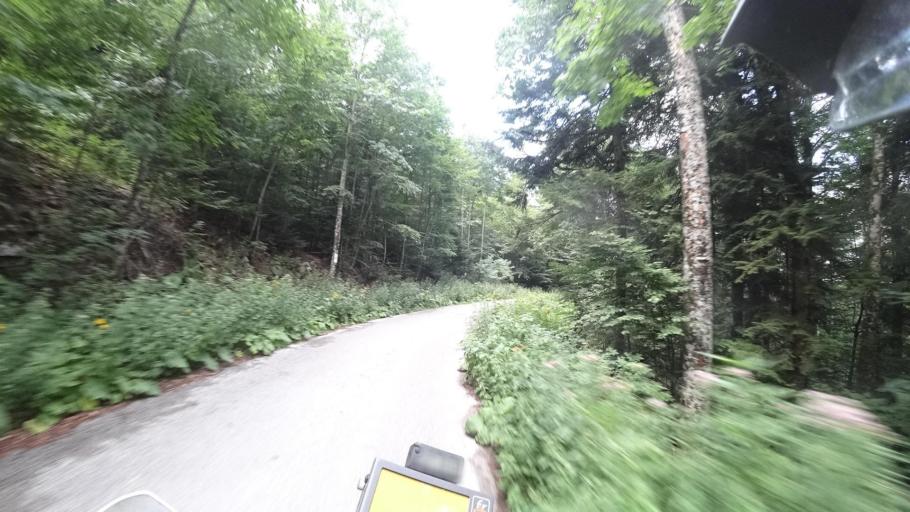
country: HR
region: Licko-Senjska
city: Senj
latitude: 45.1128
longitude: 14.9452
